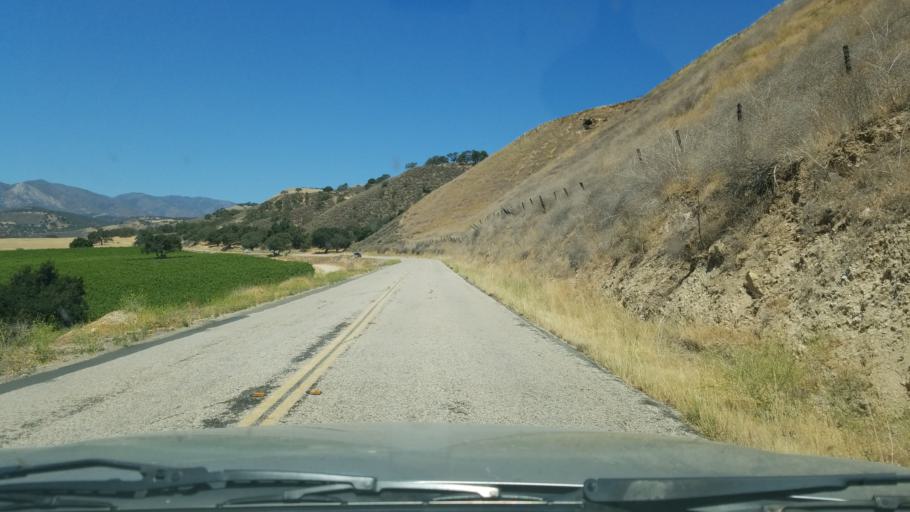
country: US
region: California
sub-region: Monterey County
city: Greenfield
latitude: 36.2667
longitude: -121.3694
